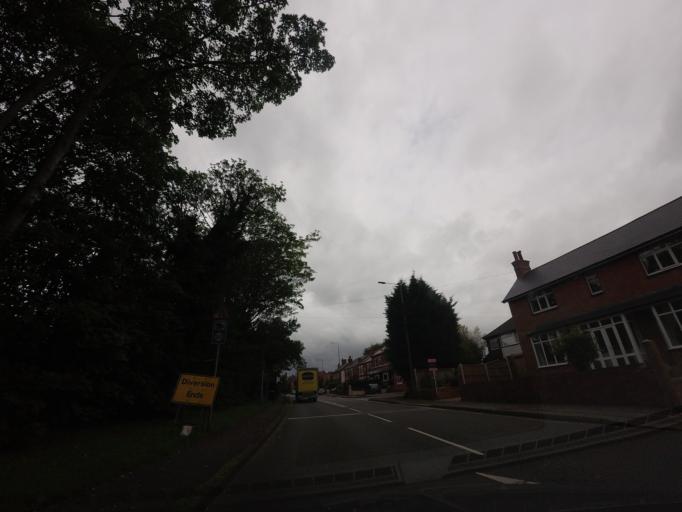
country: GB
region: England
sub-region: Nottinghamshire
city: Kimberley
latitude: 52.9992
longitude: -1.2405
